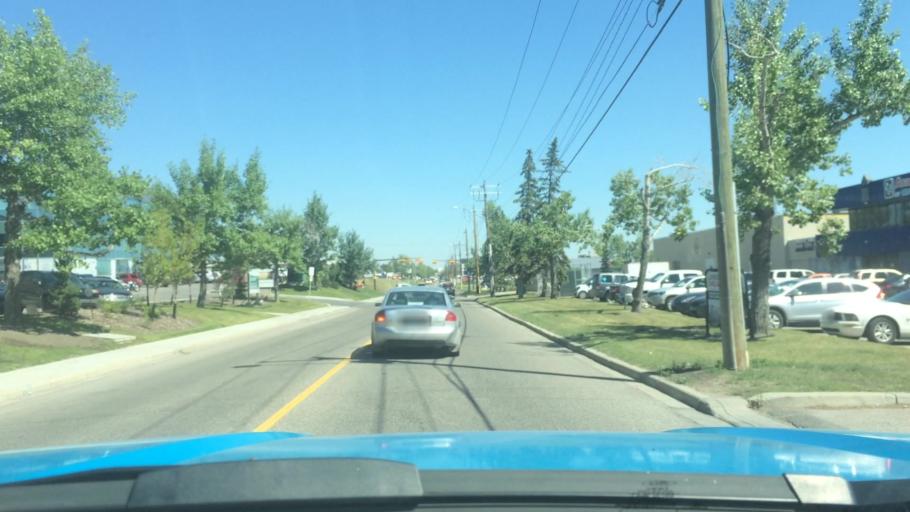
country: CA
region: Alberta
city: Calgary
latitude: 51.0556
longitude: -113.9860
